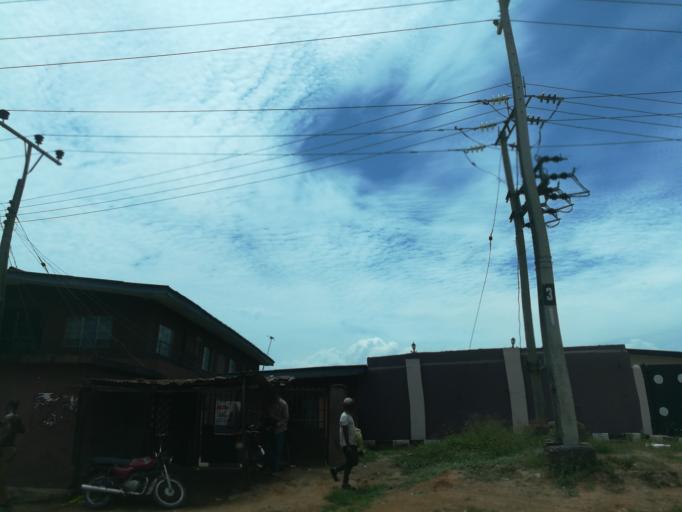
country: NG
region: Lagos
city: Ebute Ikorodu
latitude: 6.5986
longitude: 3.4935
